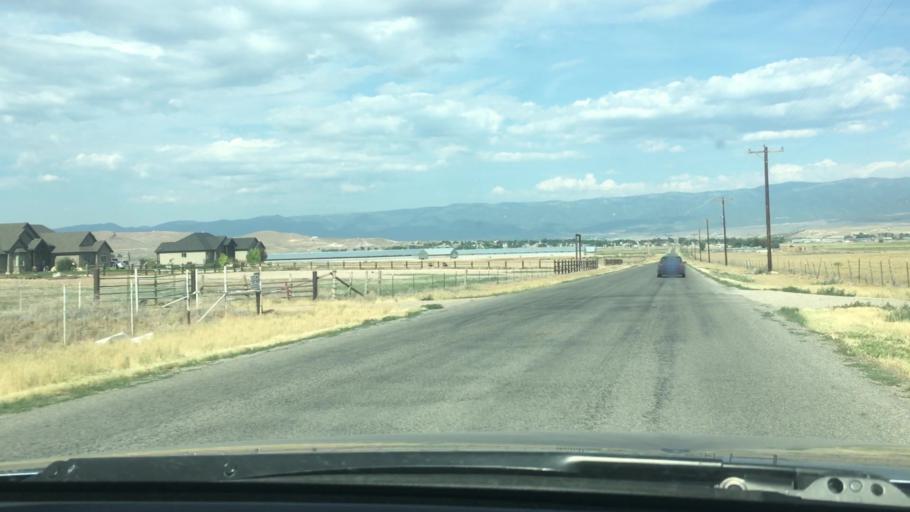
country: US
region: Utah
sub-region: Sanpete County
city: Moroni
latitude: 39.5235
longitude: -111.6256
